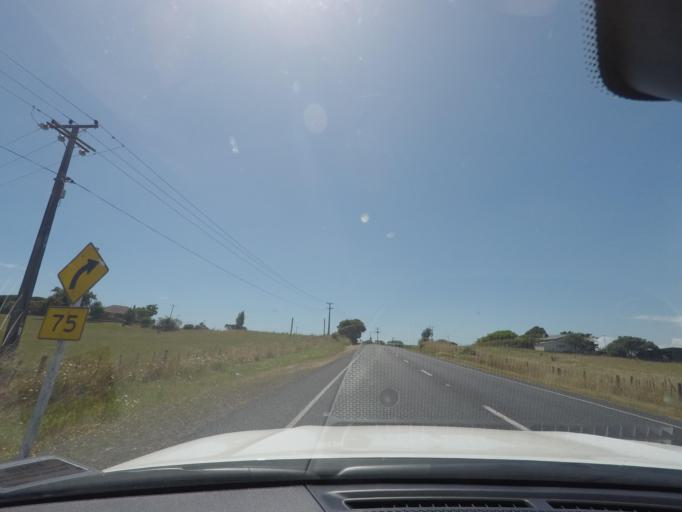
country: NZ
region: Auckland
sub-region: Auckland
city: Parakai
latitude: -36.6960
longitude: 174.4302
